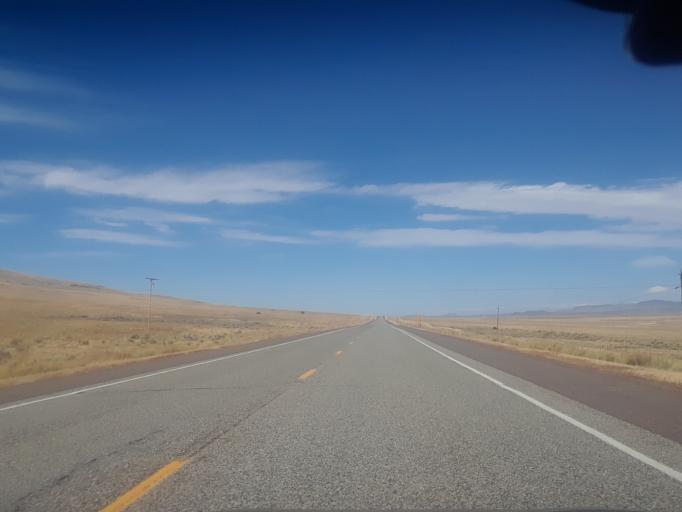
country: US
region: Colorado
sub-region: Conejos County
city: Conejos
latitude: 36.8415
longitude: -105.9728
